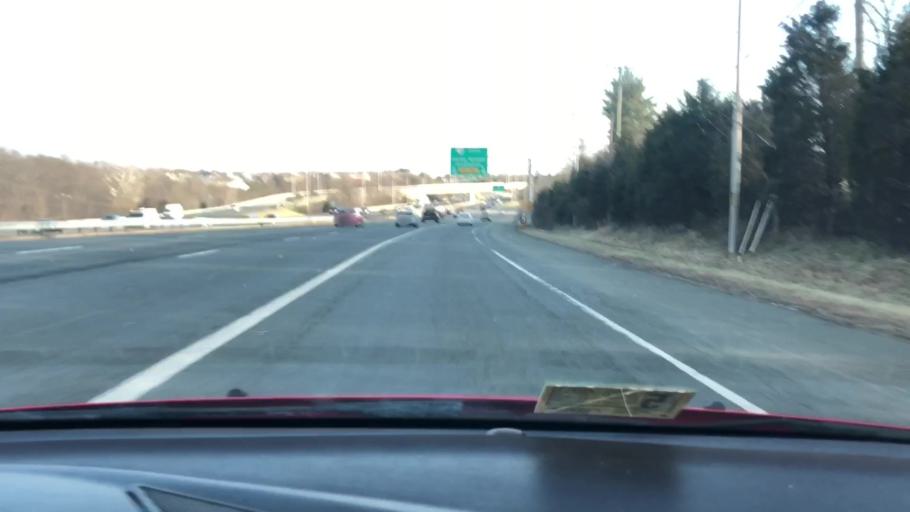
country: US
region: Virginia
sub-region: Loudoun County
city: University Center
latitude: 39.0483
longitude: -77.4352
